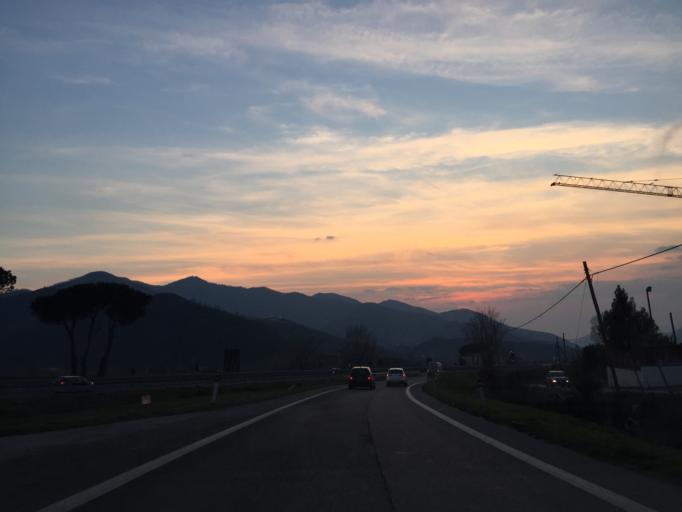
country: IT
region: Campania
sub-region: Provincia di Salerno
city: Lancusi-Penta-Bolano
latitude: 40.7728
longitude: 14.7824
